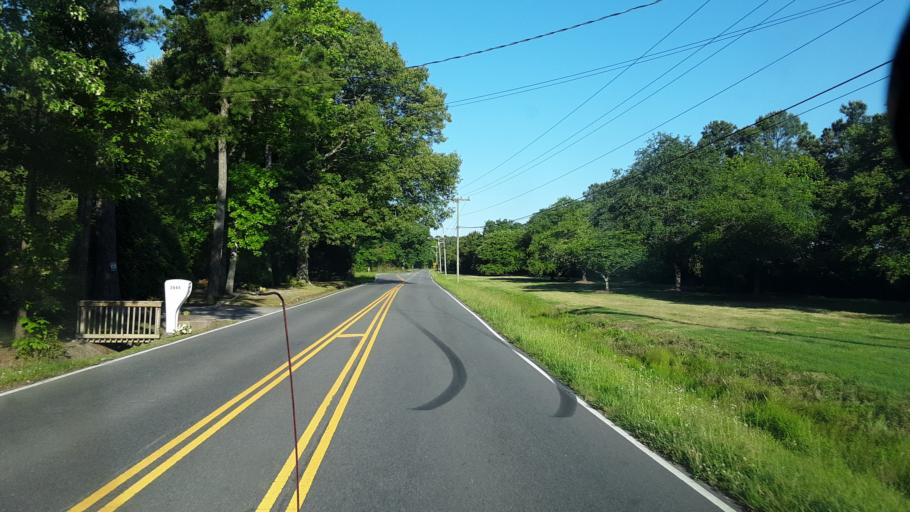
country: US
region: Virginia
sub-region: City of Virginia Beach
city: Virginia Beach
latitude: 36.7230
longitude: -76.0604
